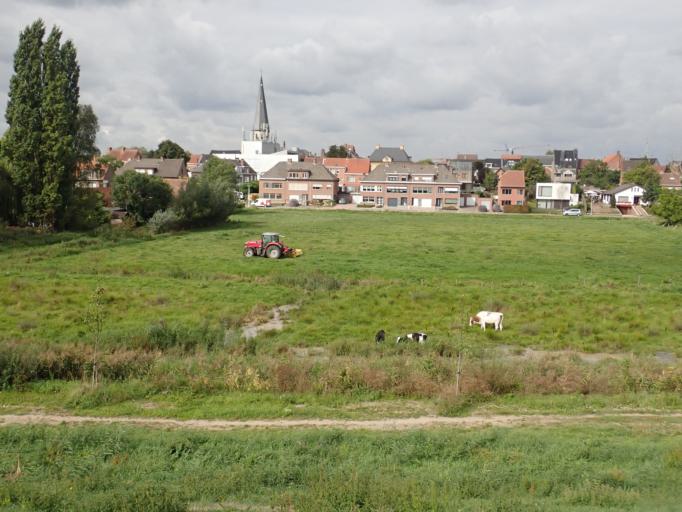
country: BE
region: Flanders
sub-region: Provincie Oost-Vlaanderen
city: Kruibeke
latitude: 51.1709
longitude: 4.3176
